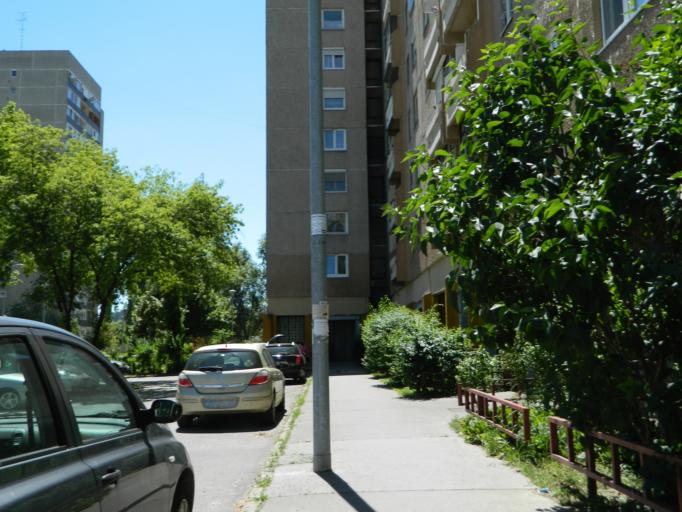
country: HU
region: Pest
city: Budakalasz
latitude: 47.6014
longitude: 19.0532
